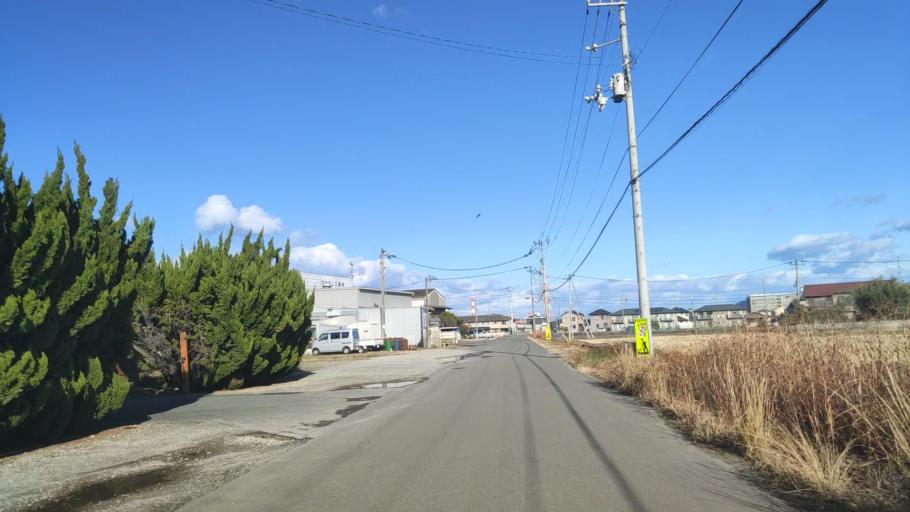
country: JP
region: Ehime
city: Saijo
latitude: 33.9213
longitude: 133.1602
